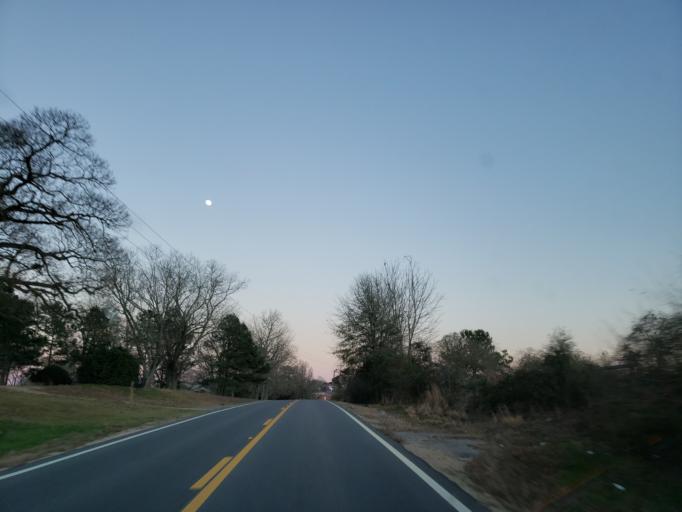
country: US
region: Mississippi
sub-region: Jones County
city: Ellisville
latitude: 31.5799
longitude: -89.2775
